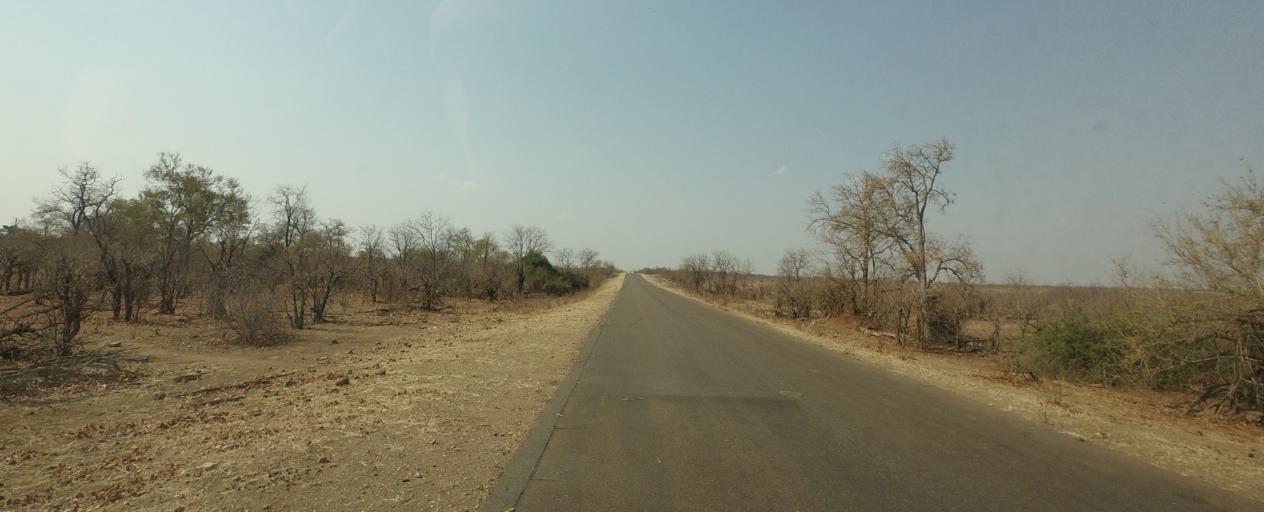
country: ZA
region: Limpopo
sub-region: Mopani District Municipality
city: Giyani
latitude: -23.1303
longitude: 31.3798
